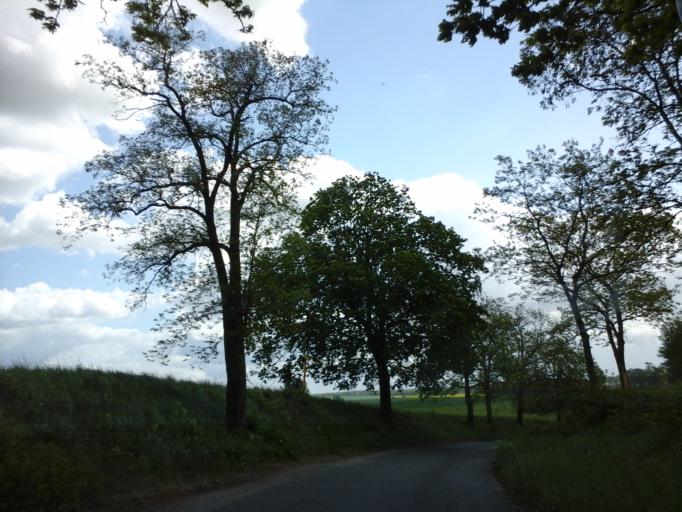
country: PL
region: West Pomeranian Voivodeship
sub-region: Powiat choszczenski
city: Choszczno
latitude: 53.1228
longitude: 15.3972
